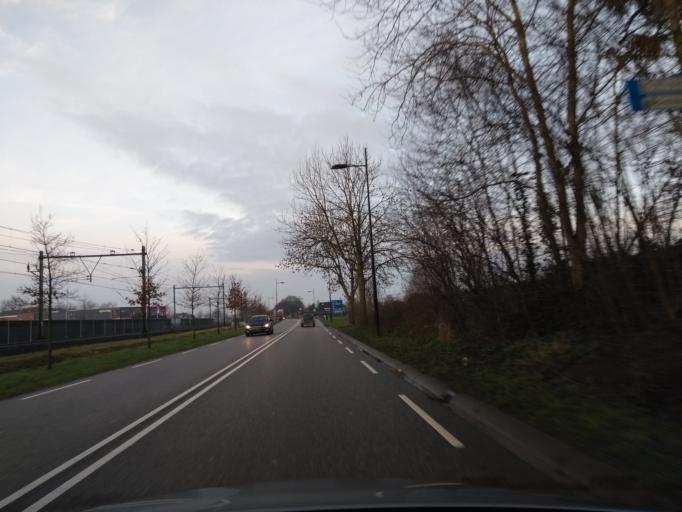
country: NL
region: Overijssel
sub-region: Gemeente Hof van Twente
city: Markelo
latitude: 52.3108
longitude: 6.5141
